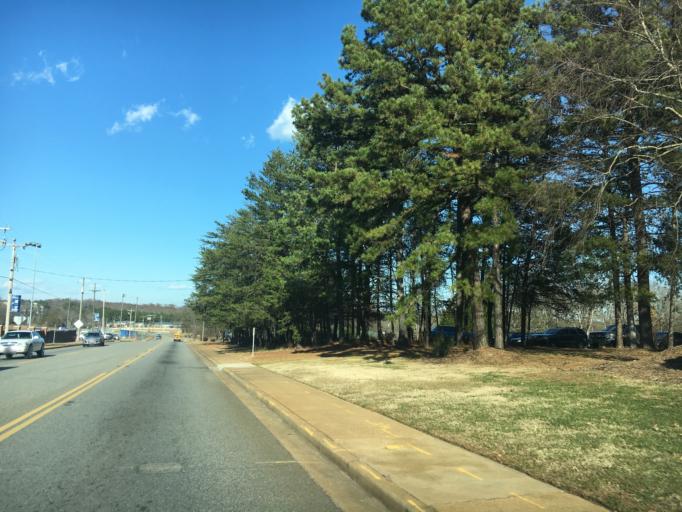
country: US
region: South Carolina
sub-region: Spartanburg County
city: Lyman
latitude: 34.9318
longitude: -82.1257
